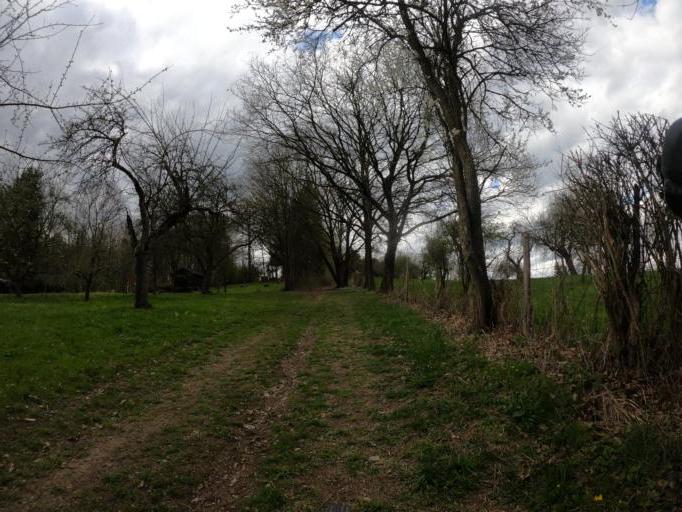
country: DE
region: Baden-Wuerttemberg
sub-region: Tuebingen Region
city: Wannweil
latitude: 48.4877
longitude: 9.1658
